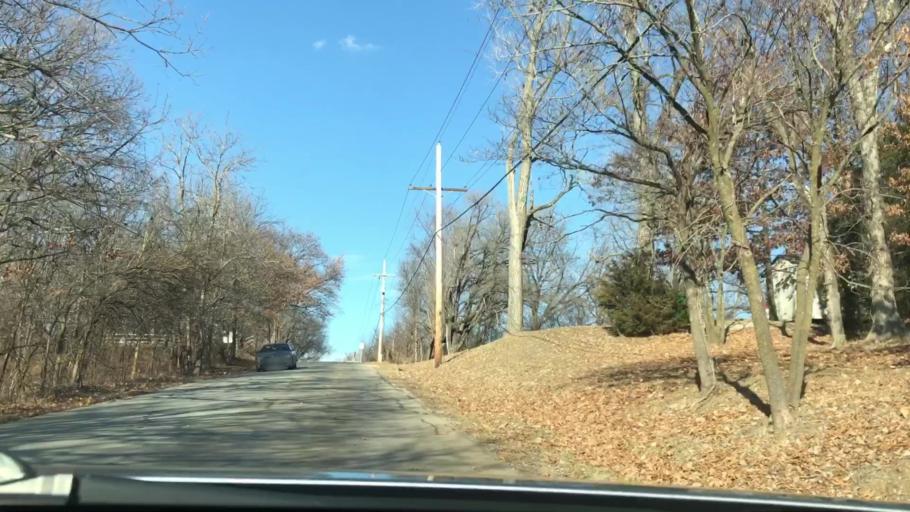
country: US
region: Missouri
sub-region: Platte County
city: Parkville
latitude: 39.2003
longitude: -94.6872
